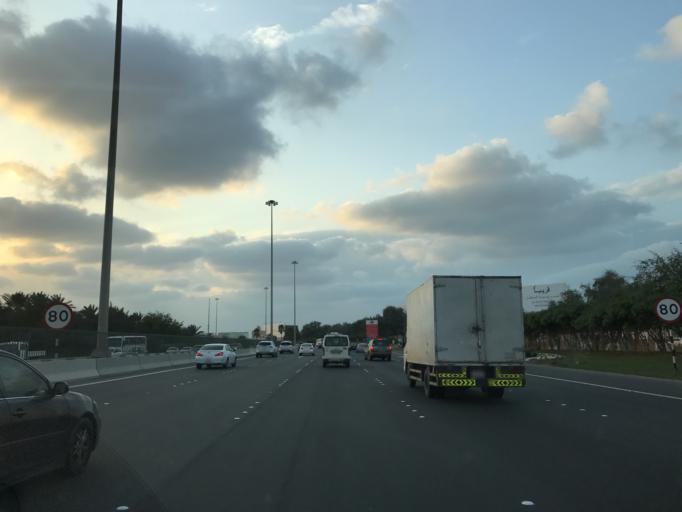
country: AE
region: Abu Dhabi
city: Abu Dhabi
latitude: 24.4197
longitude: 54.4925
